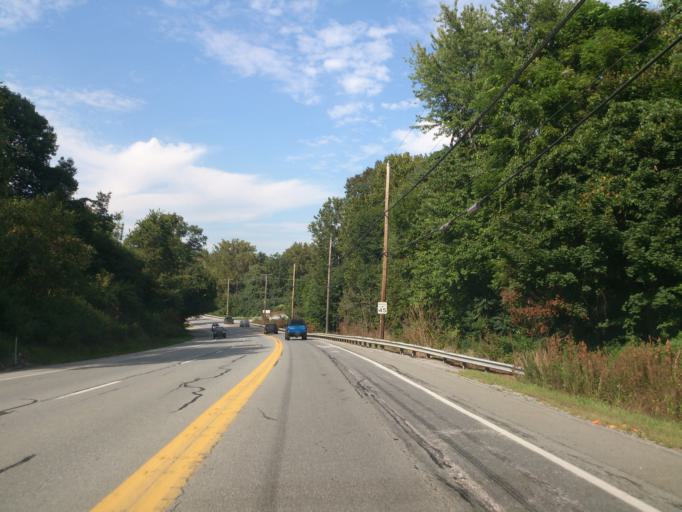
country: US
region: Pennsylvania
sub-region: York County
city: Wrightsville
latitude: 40.0126
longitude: -76.5406
